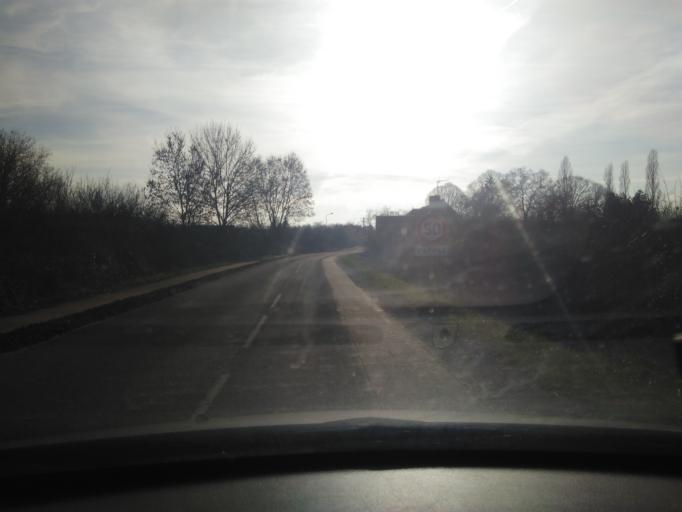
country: FR
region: Bourgogne
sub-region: Departement de la Nievre
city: Saint-Parize-le-Chatel
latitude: 46.8235
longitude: 3.2470
